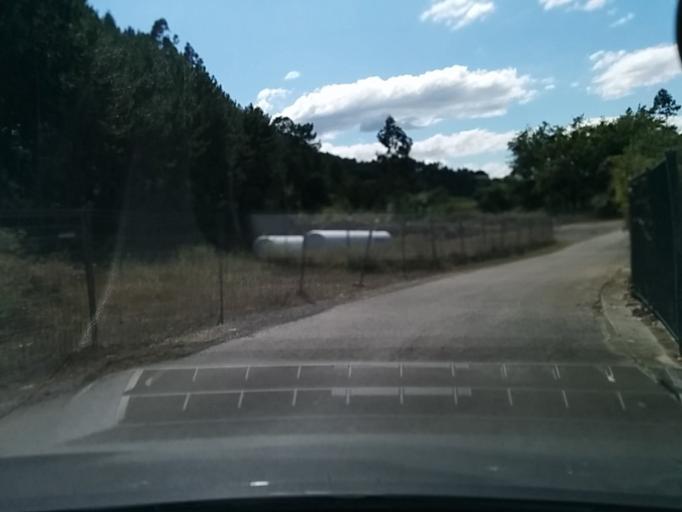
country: ES
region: Basque Country
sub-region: Bizkaia
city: Mendexa
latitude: 43.3442
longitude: -2.4800
